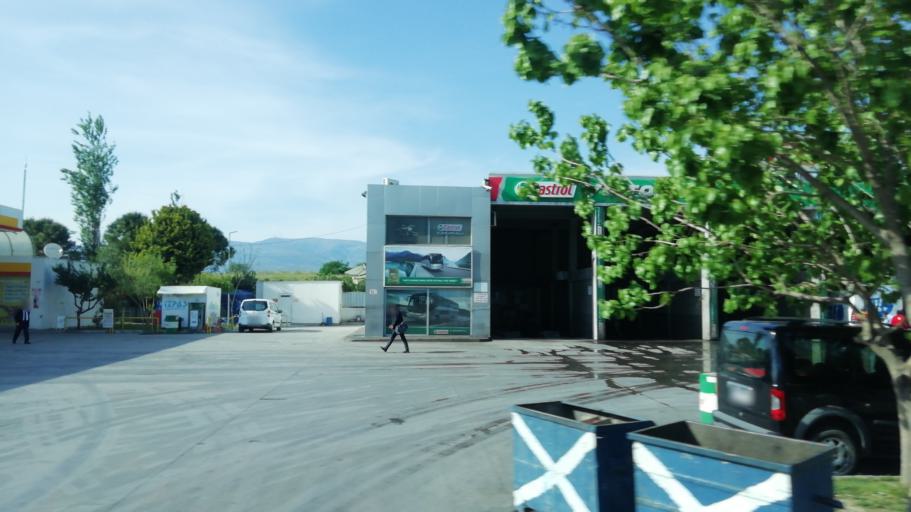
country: TR
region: Izmir
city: Bornova
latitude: 38.4323
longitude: 27.2136
